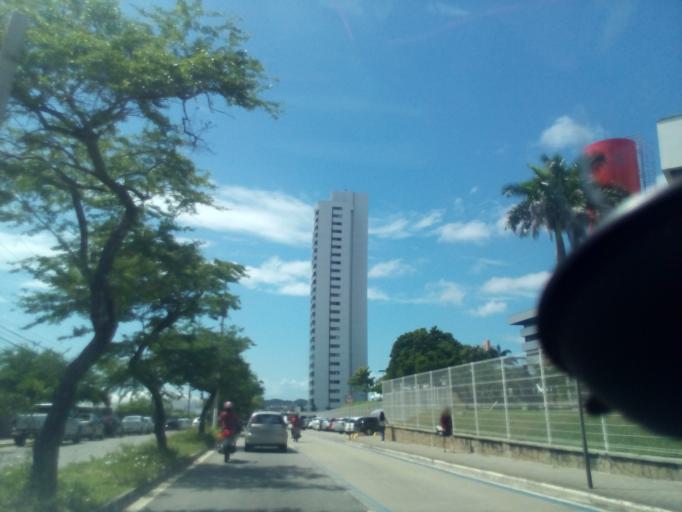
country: BR
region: Rio Grande do Norte
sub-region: Natal
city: Natal
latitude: -5.8249
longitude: -35.2234
